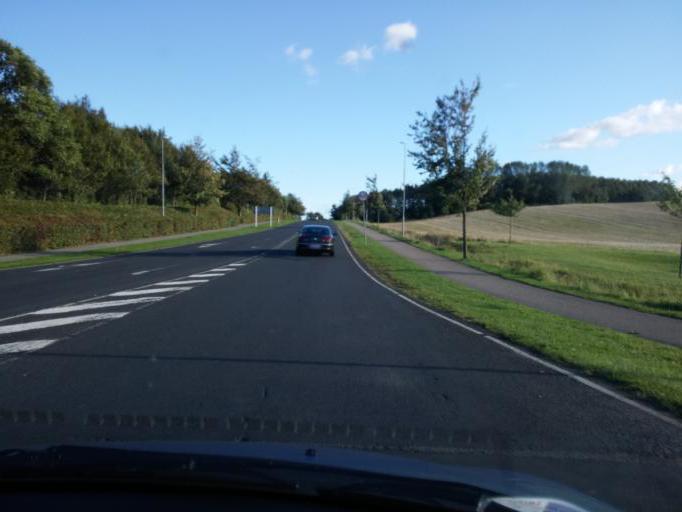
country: DK
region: South Denmark
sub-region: Kerteminde Kommune
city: Munkebo
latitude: 55.4516
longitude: 10.5404
